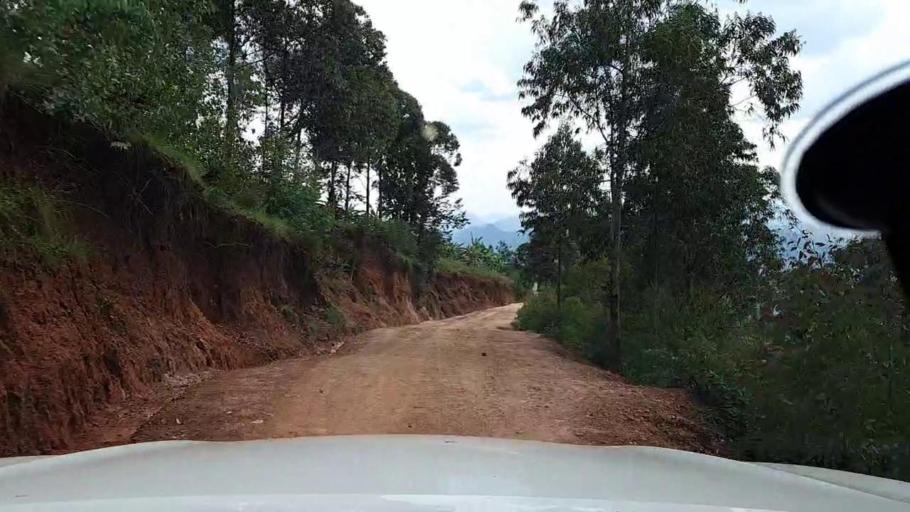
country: RW
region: Southern Province
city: Gitarama
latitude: -1.8400
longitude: 29.8231
